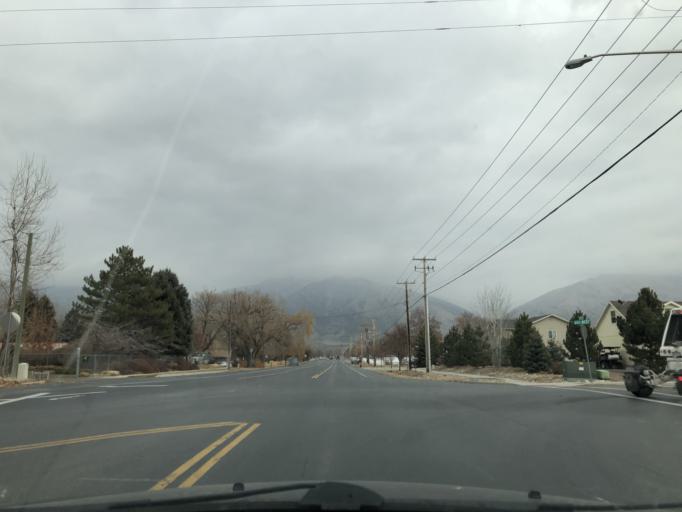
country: US
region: Utah
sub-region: Cache County
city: Nibley
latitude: 41.6749
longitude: -111.8477
